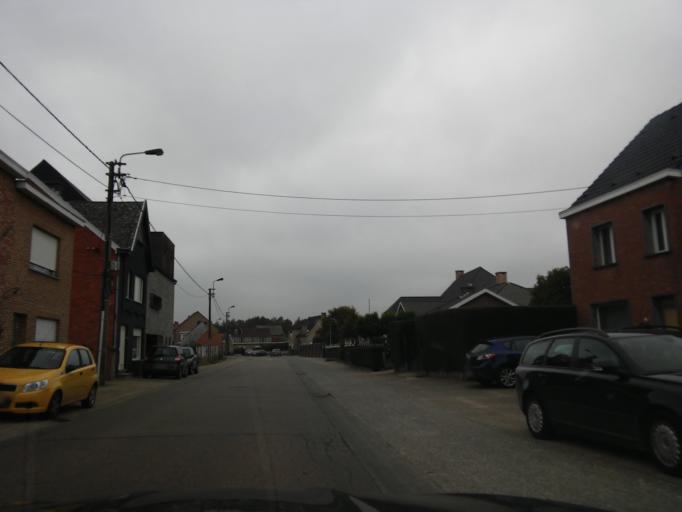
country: BE
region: Flanders
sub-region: Provincie Oost-Vlaanderen
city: Berlare
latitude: 51.0416
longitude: 4.0089
